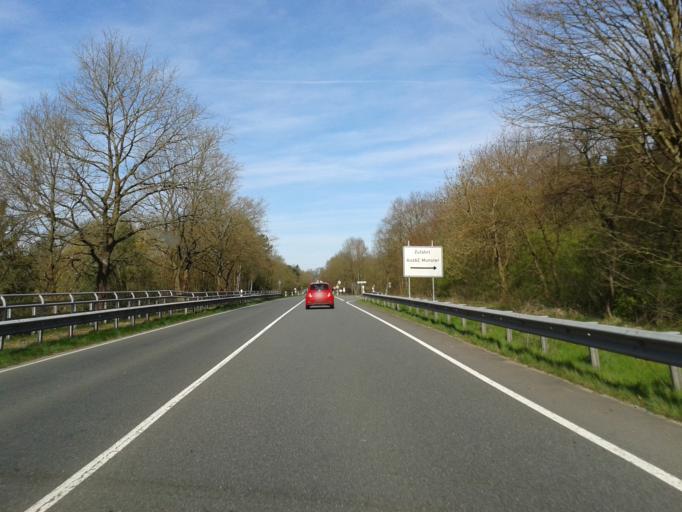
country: DE
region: Lower Saxony
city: Munster
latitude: 52.9747
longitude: 10.1024
